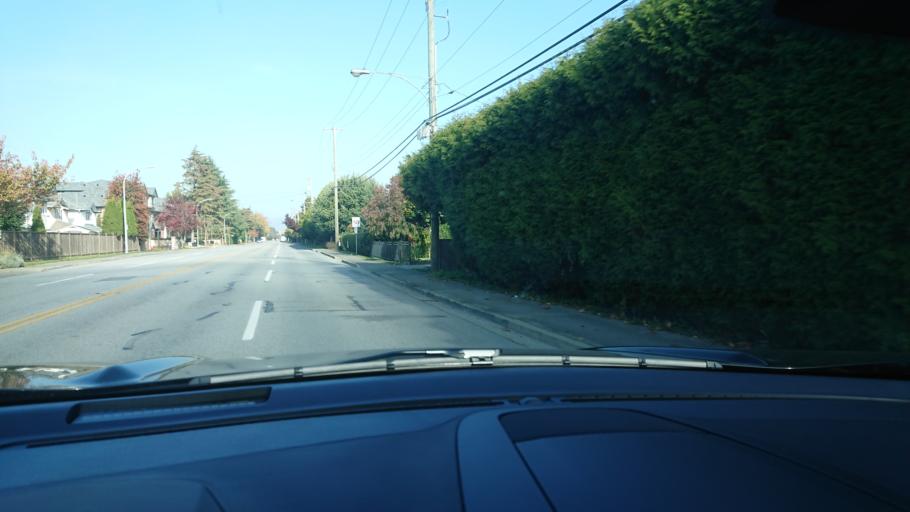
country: CA
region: British Columbia
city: Richmond
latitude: 49.1351
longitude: -123.1478
